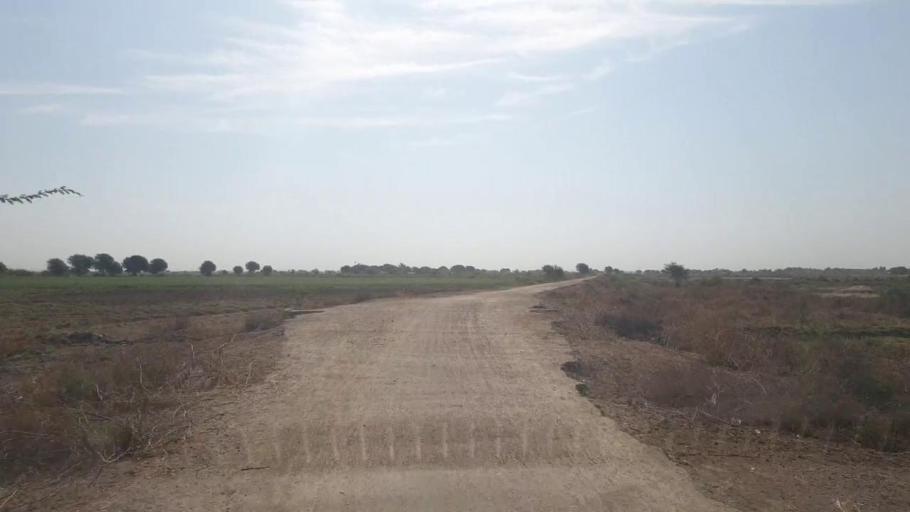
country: PK
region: Sindh
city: Umarkot
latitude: 25.2800
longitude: 69.6612
